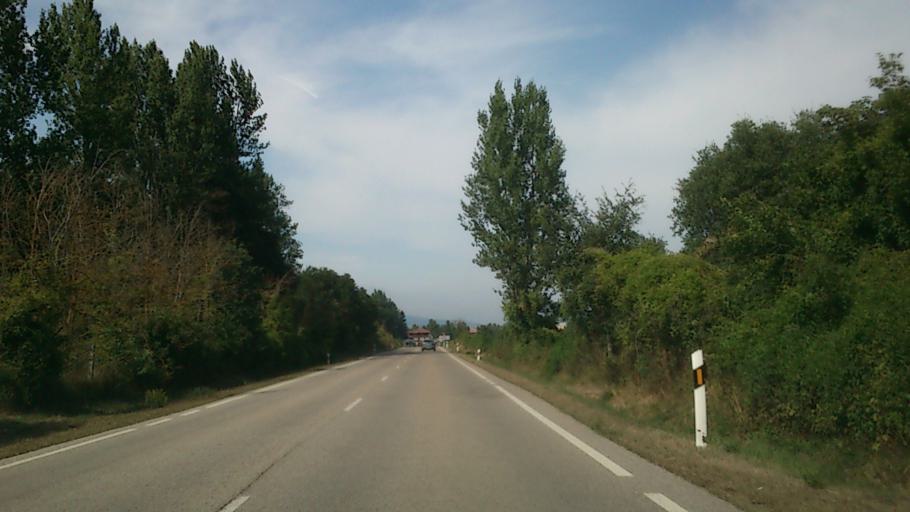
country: ES
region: Castille and Leon
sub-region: Provincia de Burgos
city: Espinosa de los Monteros
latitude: 43.0326
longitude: -3.4831
